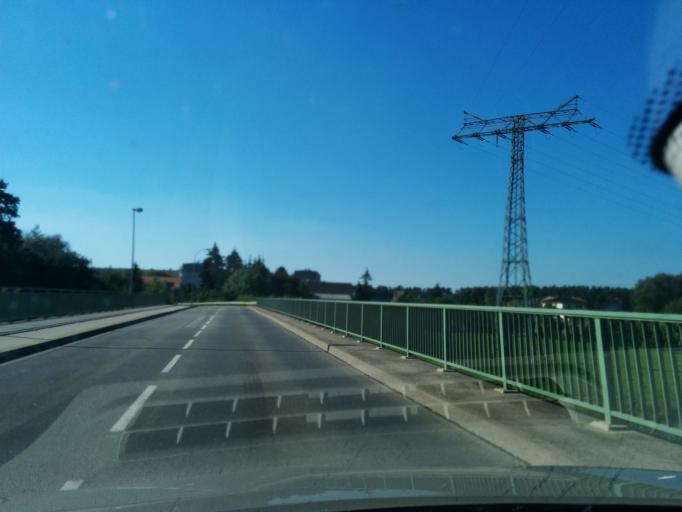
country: DE
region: Mecklenburg-Vorpommern
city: Torgelow
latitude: 53.6362
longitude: 14.0264
